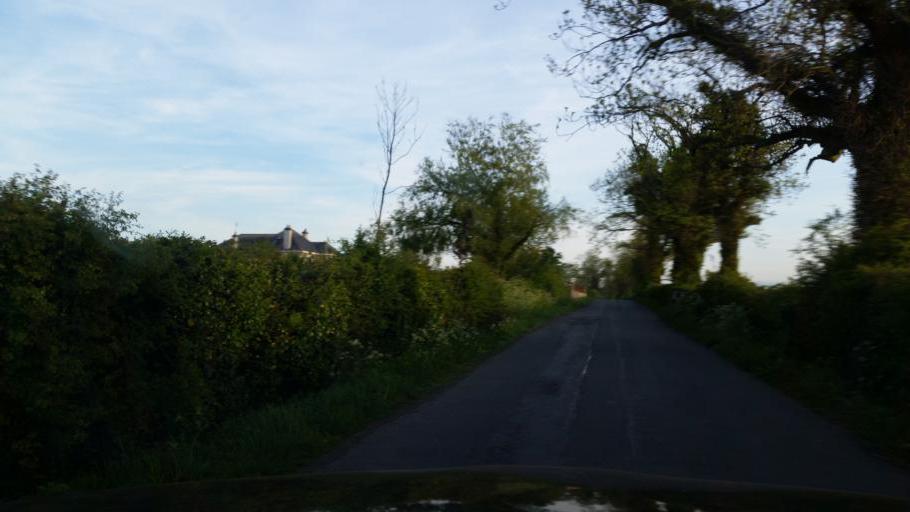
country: IE
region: Leinster
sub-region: Fingal County
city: Swords
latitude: 53.4934
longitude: -6.2137
